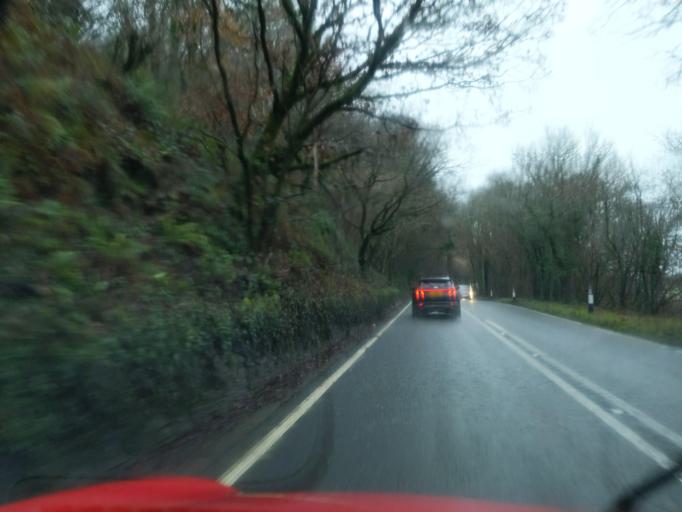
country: GB
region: England
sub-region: Cornwall
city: South Hill
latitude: 50.5691
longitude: -4.3354
